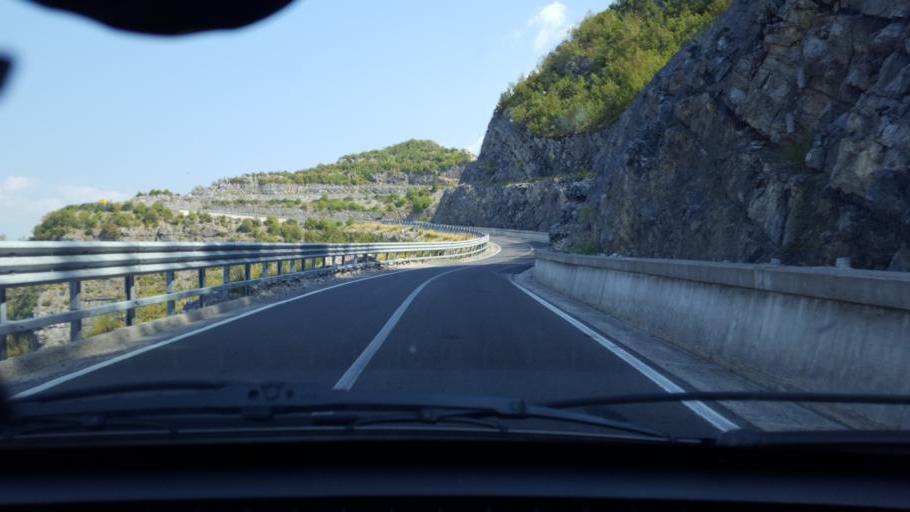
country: AL
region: Shkoder
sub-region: Rrethi i Malesia e Madhe
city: Kastrat
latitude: 42.4132
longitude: 19.4993
